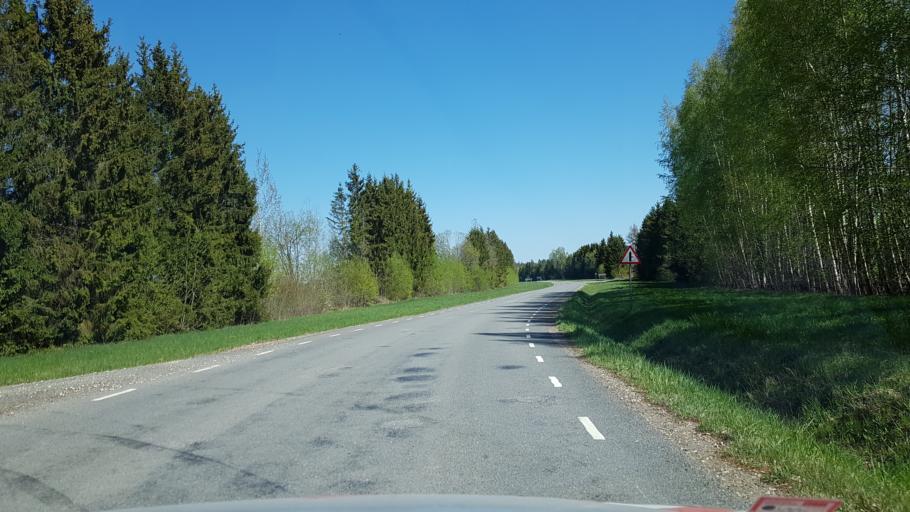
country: EE
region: Vorumaa
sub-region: Voru linn
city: Voru
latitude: 57.9505
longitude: 26.9561
